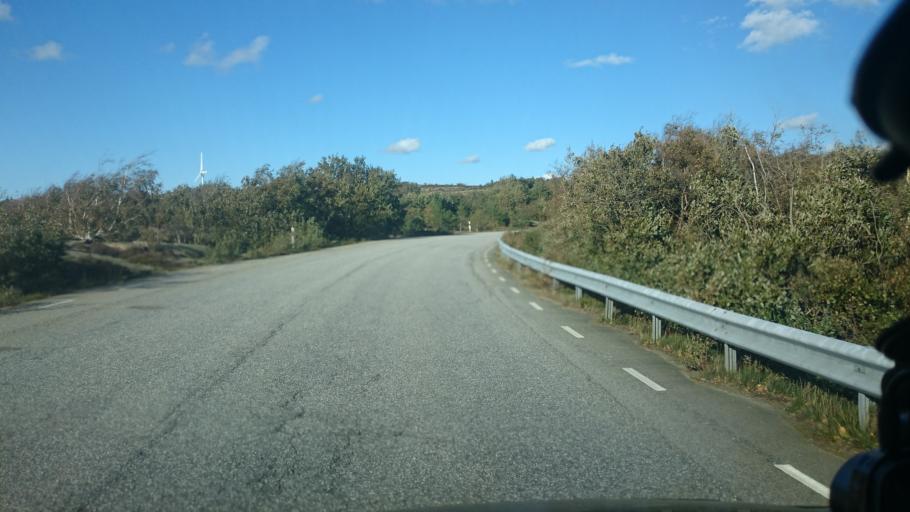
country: SE
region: Vaestra Goetaland
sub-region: Lysekils Kommun
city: Lysekil
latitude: 58.3258
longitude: 11.4156
